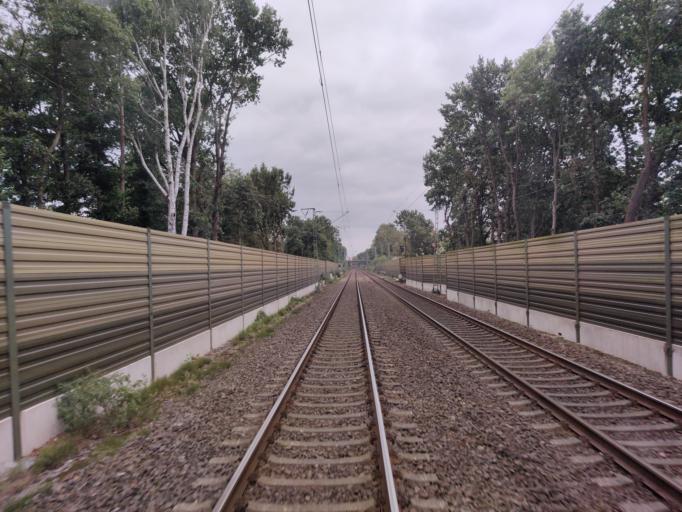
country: DE
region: Lower Saxony
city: Ritterhude
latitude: 53.1782
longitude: 8.7438
